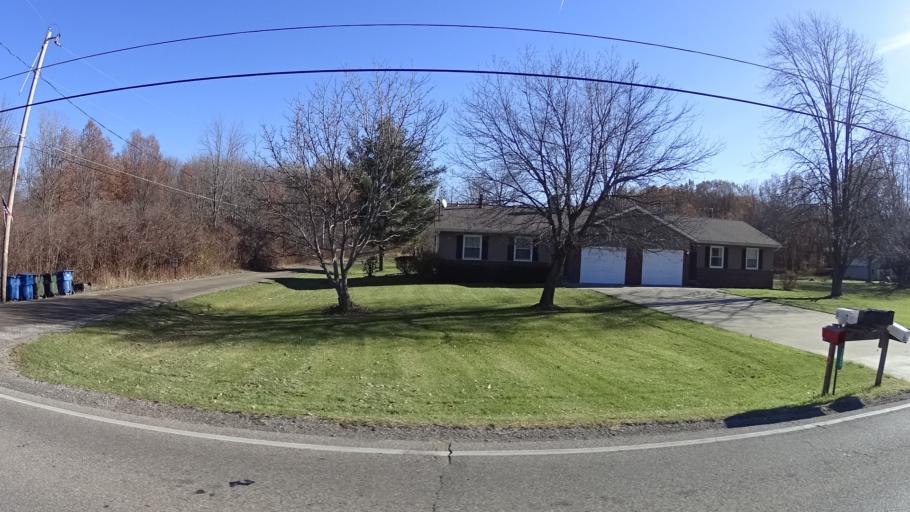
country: US
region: Ohio
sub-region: Lorain County
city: Elyria
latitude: 41.3861
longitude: -82.1500
